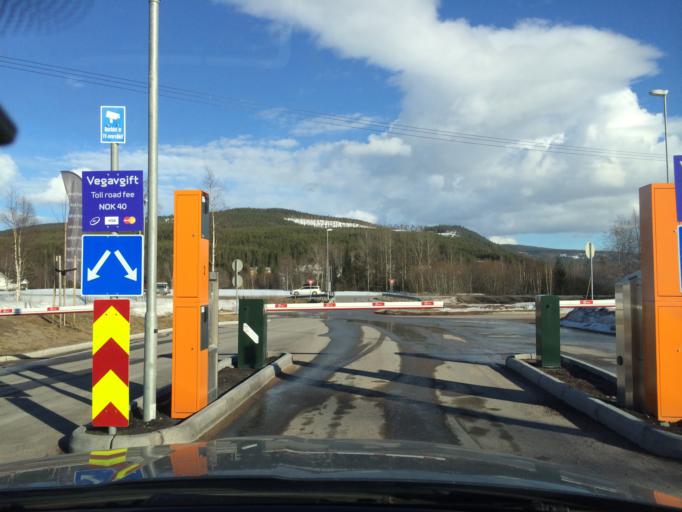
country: NO
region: Hedmark
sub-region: Trysil
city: Innbygda
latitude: 61.3417
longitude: 12.2188
